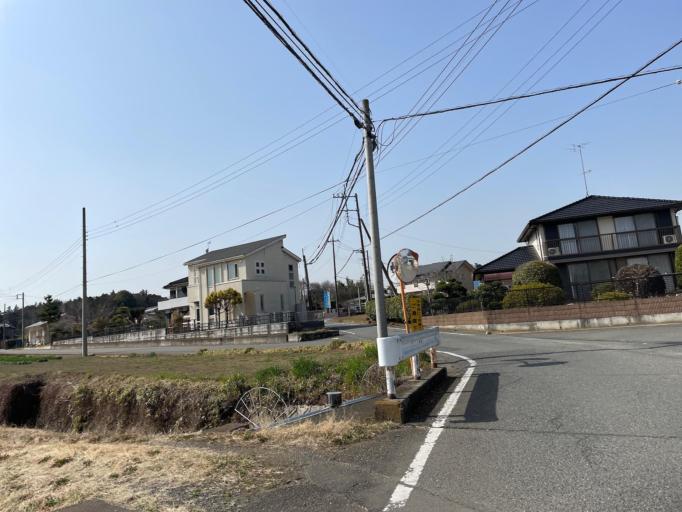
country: JP
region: Saitama
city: Yorii
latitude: 36.1099
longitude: 139.2448
